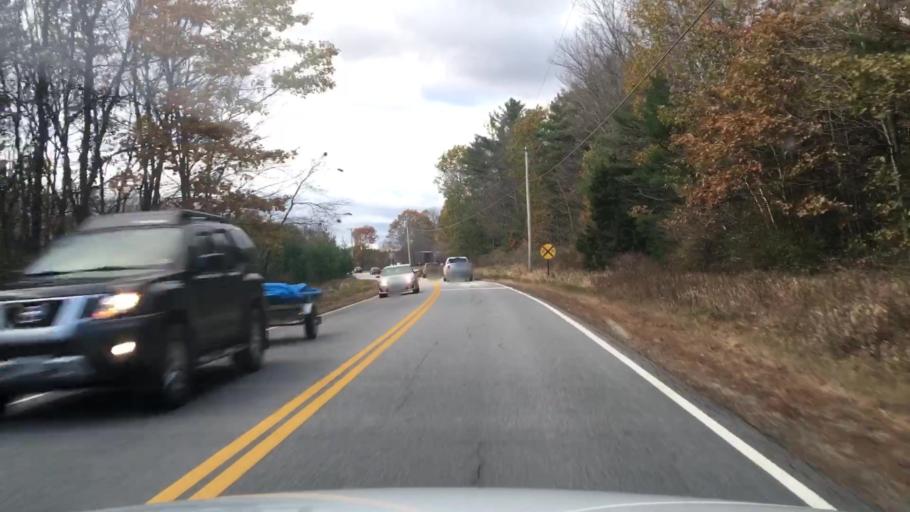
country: US
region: Maine
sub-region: Androscoggin County
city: Leeds
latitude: 44.3302
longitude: -70.1238
